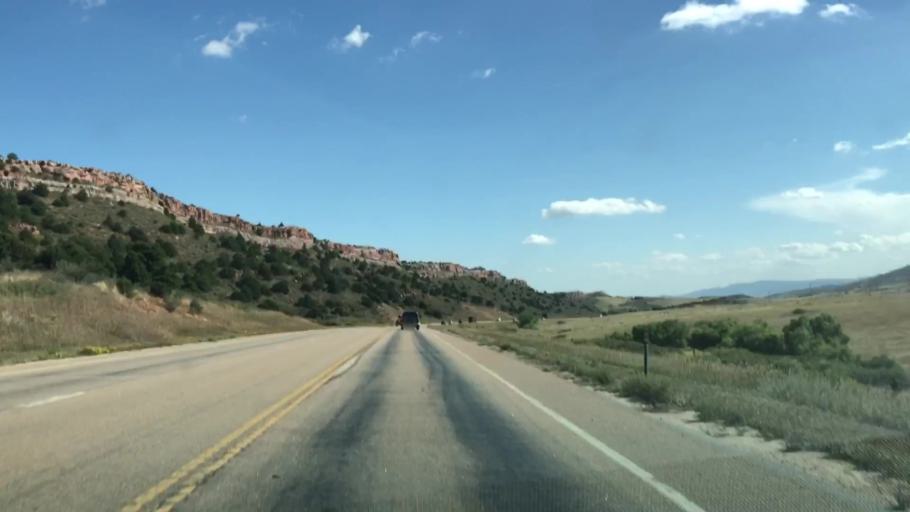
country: US
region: Colorado
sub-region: Larimer County
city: Laporte
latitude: 40.7799
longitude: -105.1867
